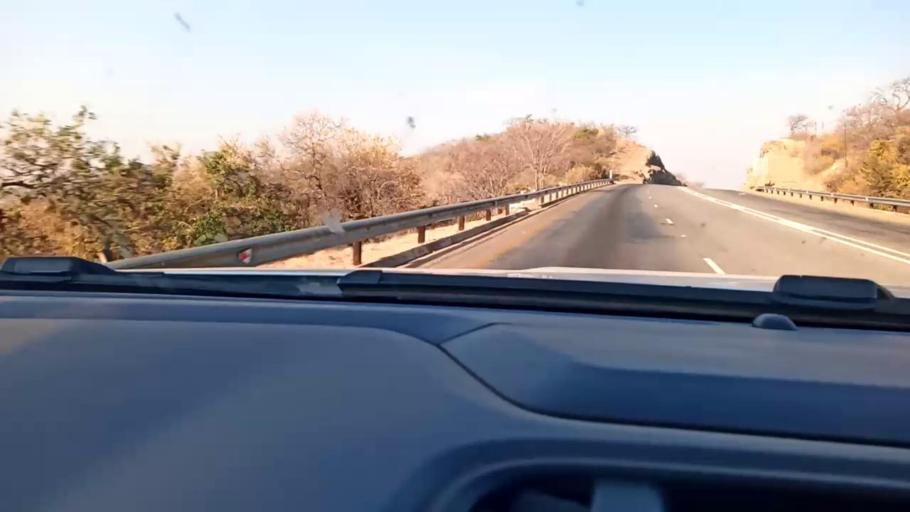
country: ZA
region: Limpopo
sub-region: Mopani District Municipality
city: Duiwelskloof
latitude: -23.6369
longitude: 30.1475
